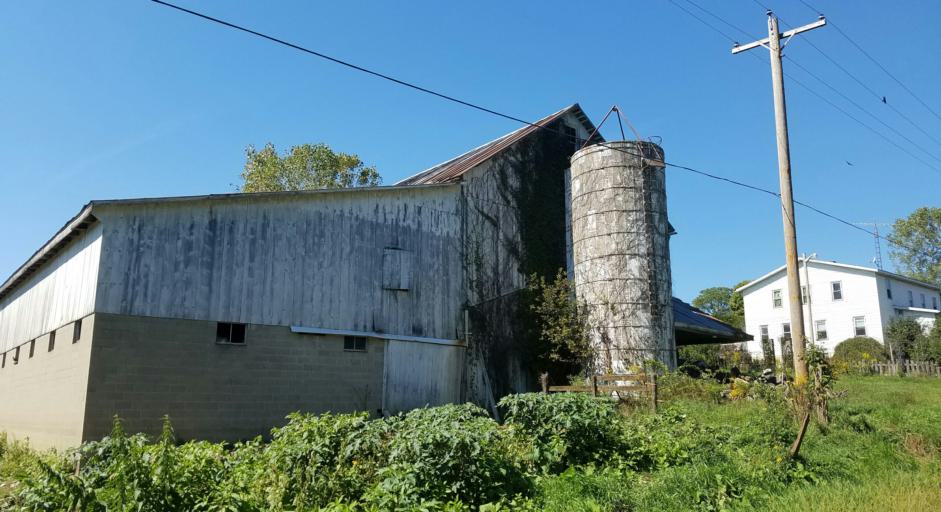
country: US
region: Ohio
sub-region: Knox County
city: Danville
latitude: 40.5545
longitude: -82.3464
